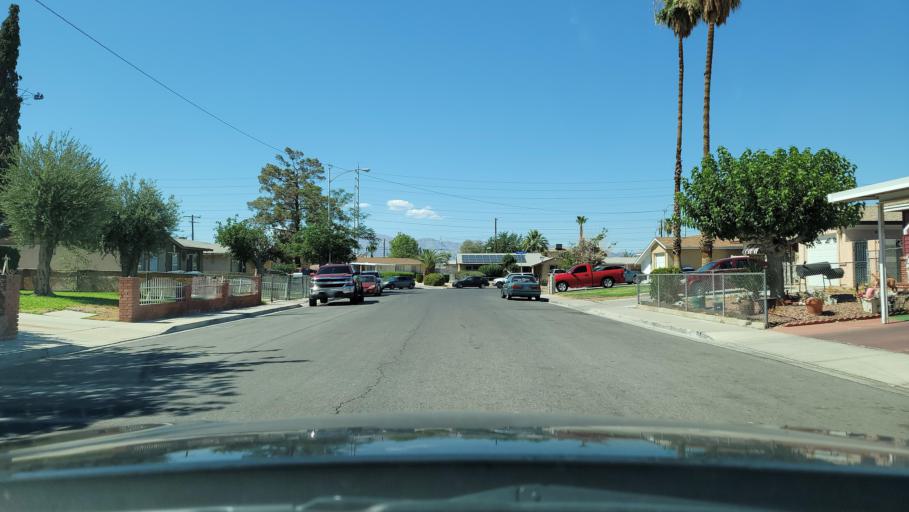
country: US
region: Nevada
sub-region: Clark County
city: Las Vegas
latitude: 36.2007
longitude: -115.1510
